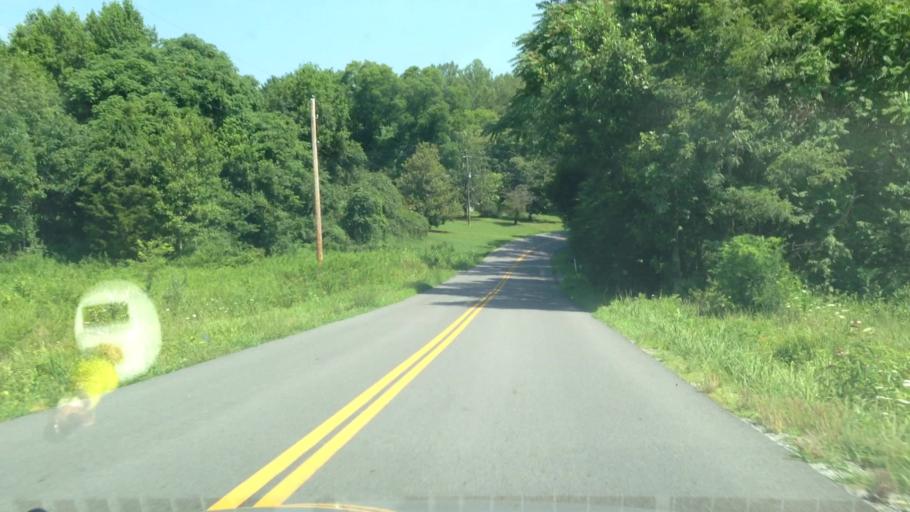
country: US
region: Virginia
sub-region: Patrick County
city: Patrick Springs
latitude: 36.5912
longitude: -80.1781
